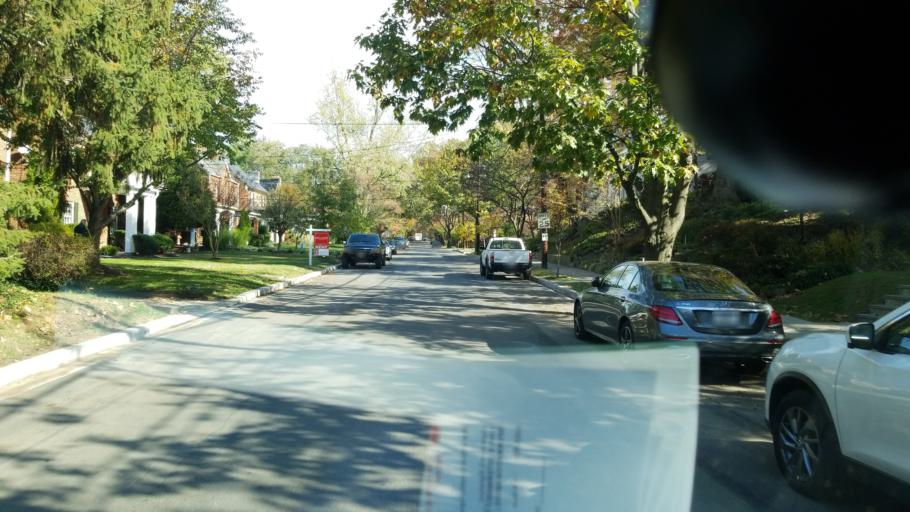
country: US
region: Maryland
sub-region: Montgomery County
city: Chevy Chase
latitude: 38.9728
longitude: -77.0595
